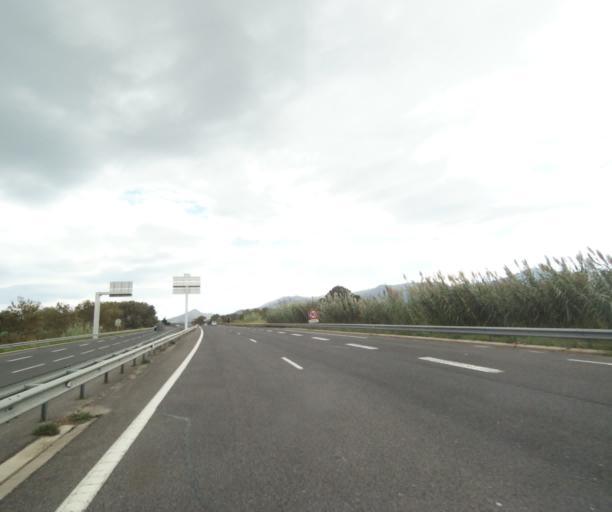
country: FR
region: Languedoc-Roussillon
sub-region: Departement des Pyrenees-Orientales
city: Elne
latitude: 42.5872
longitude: 2.9835
